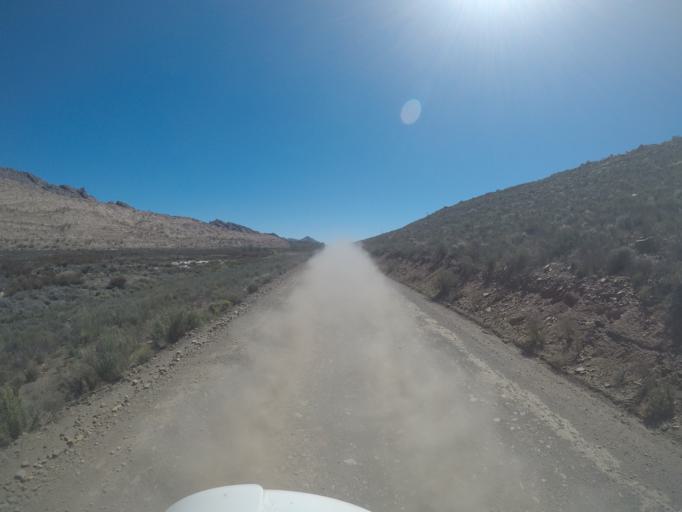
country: ZA
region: Western Cape
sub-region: Cape Winelands District Municipality
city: Ceres
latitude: -32.8221
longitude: 19.4532
